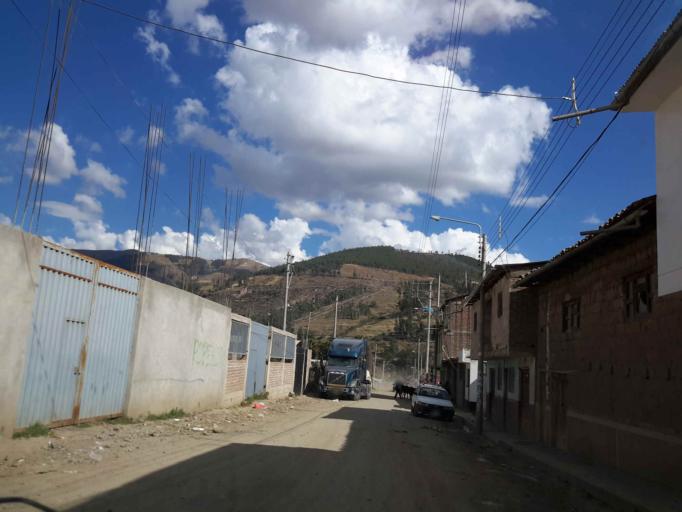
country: PE
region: Apurimac
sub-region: Provincia de Andahuaylas
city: Talavera
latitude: -13.6542
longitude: -73.4312
